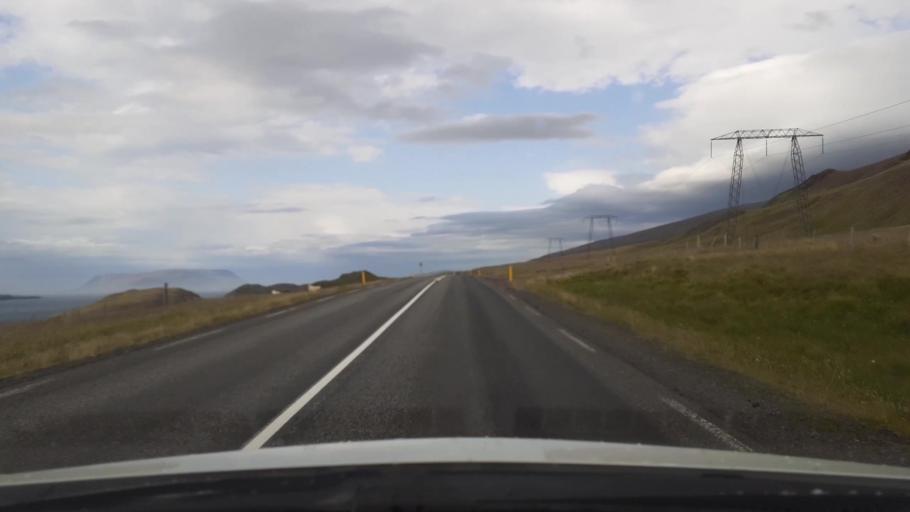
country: IS
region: Capital Region
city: Mosfellsbaer
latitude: 64.3988
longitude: -21.4745
